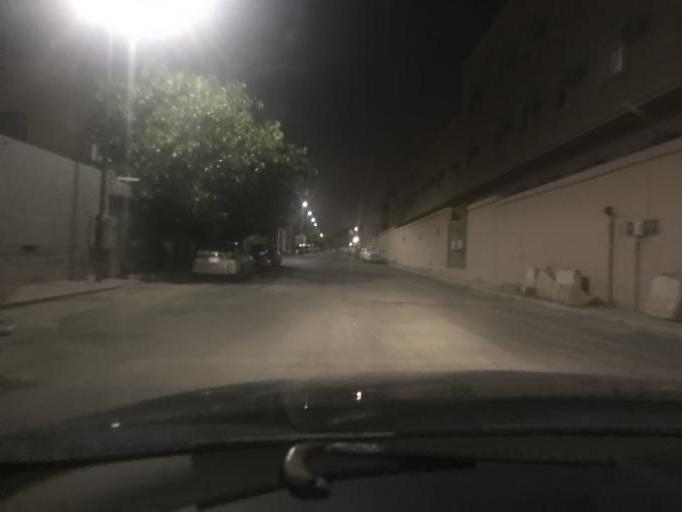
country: SA
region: Ar Riyad
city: Riyadh
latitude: 24.7267
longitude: 46.7653
